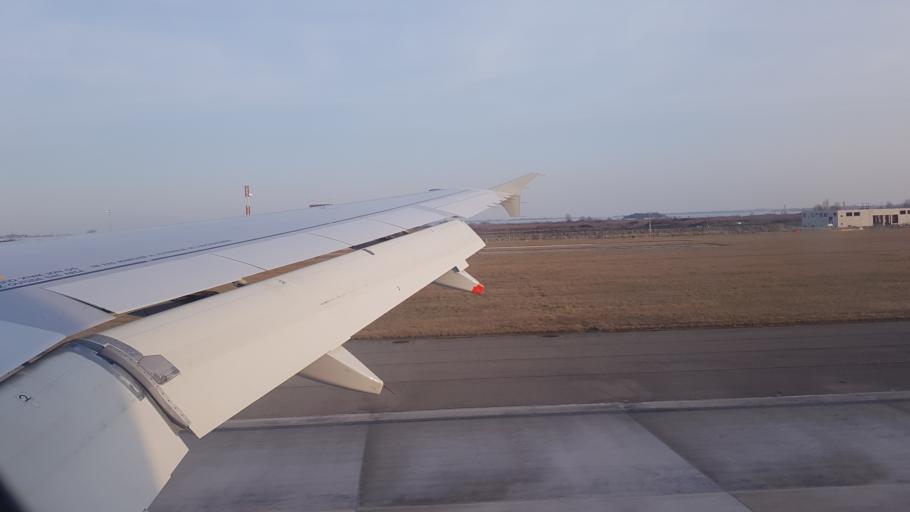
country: IT
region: Veneto
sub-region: Provincia di Venezia
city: Tessera
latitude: 45.4961
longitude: 12.3399
